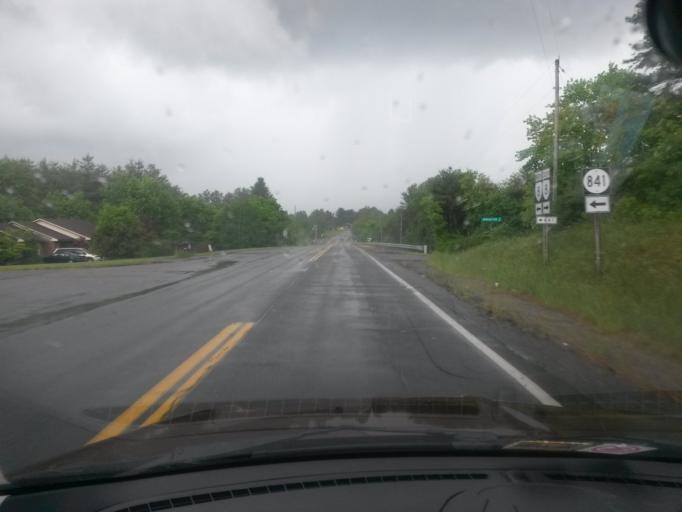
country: US
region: Virginia
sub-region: Floyd County
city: Floyd
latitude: 36.9700
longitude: -80.3885
